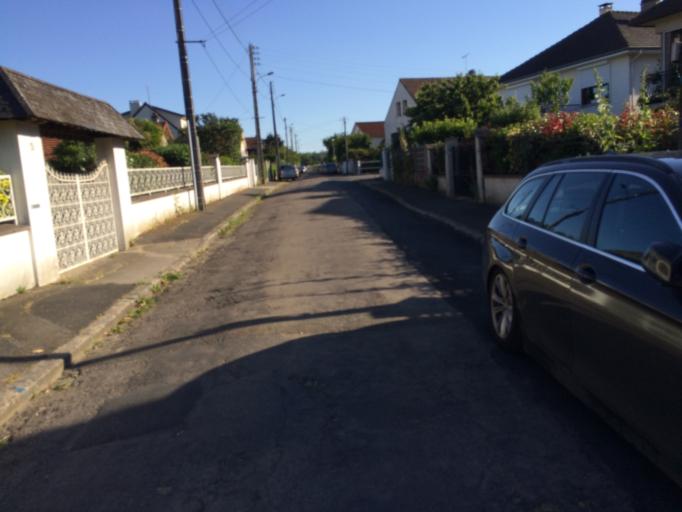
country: FR
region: Ile-de-France
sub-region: Departement de l'Essonne
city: Igny
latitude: 48.7278
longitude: 2.2193
